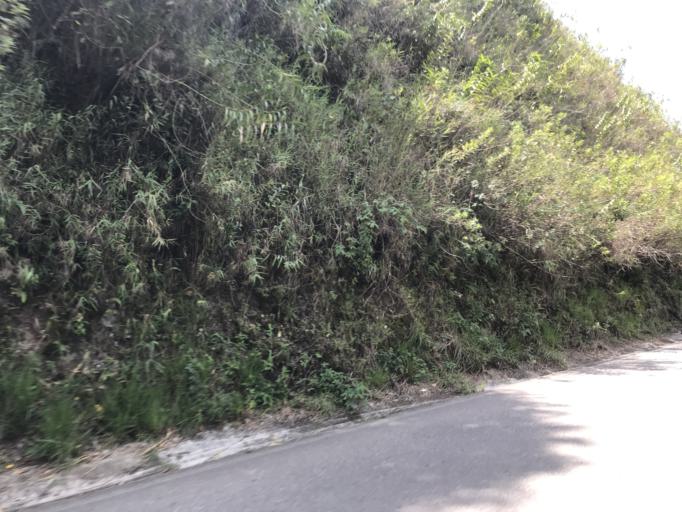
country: CO
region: Huila
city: San Agustin
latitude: 1.8760
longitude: -76.2443
